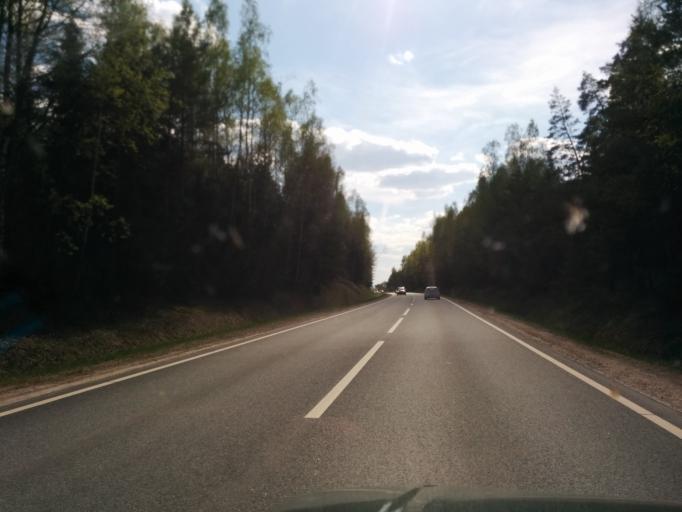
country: LV
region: Sigulda
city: Sigulda
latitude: 57.2778
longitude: 24.9027
